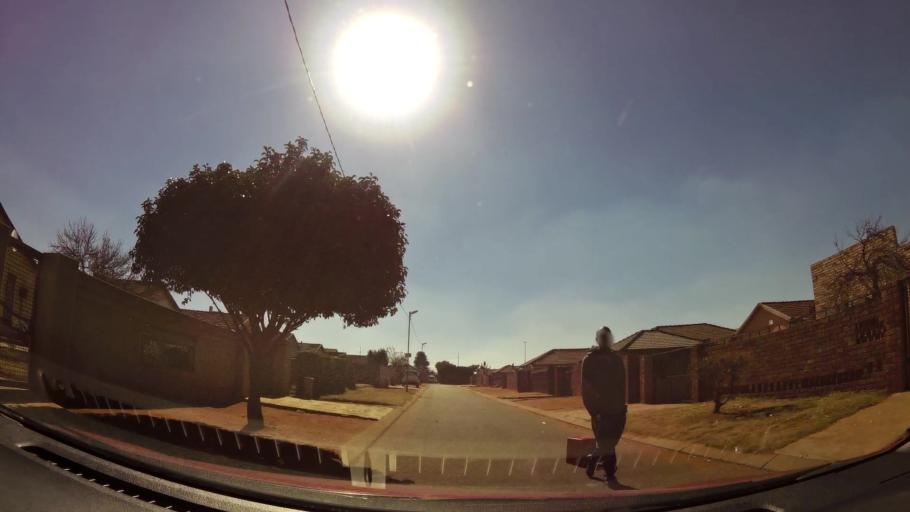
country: ZA
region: Gauteng
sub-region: City of Johannesburg Metropolitan Municipality
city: Soweto
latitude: -26.2438
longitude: 27.8057
